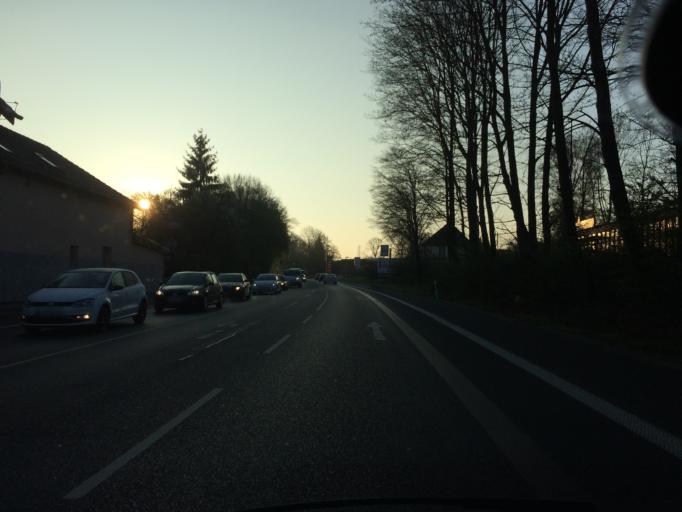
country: DE
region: North Rhine-Westphalia
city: Hattingen
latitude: 51.4461
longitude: 7.1572
